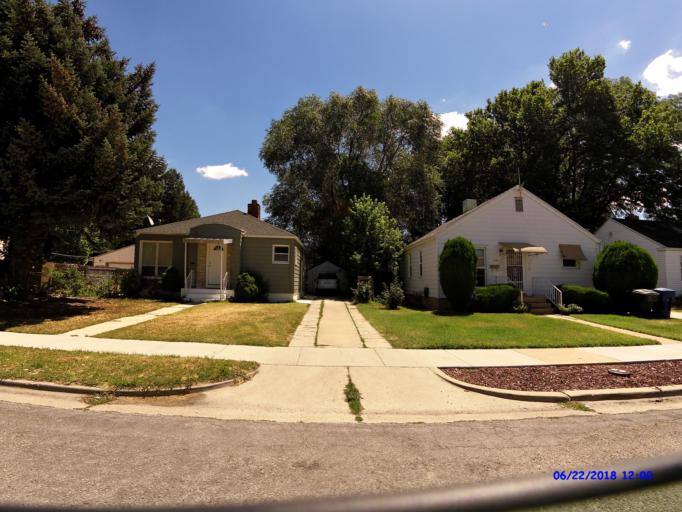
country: US
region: Utah
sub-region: Weber County
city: Ogden
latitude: 41.2389
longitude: -111.9743
